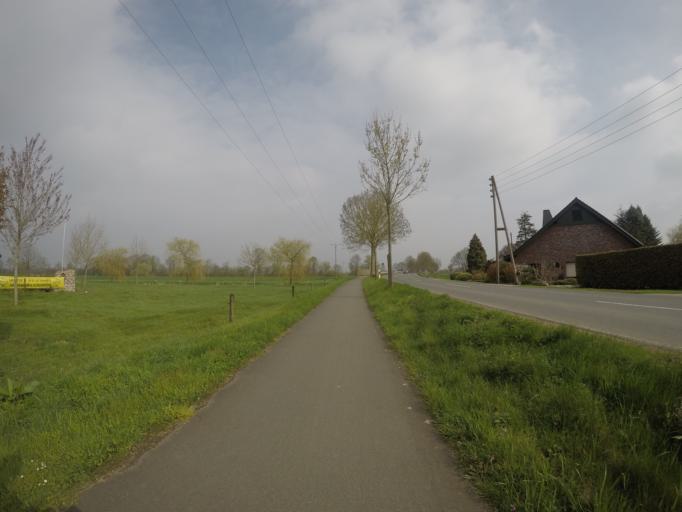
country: DE
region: North Rhine-Westphalia
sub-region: Regierungsbezirk Munster
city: Isselburg
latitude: 51.8443
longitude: 6.5017
